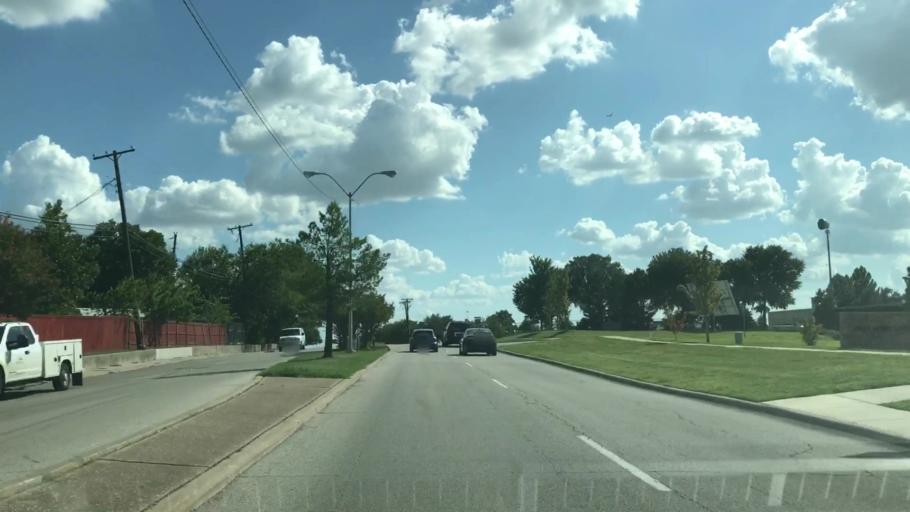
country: US
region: Texas
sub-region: Dallas County
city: Irving
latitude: 32.8457
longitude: -97.0089
